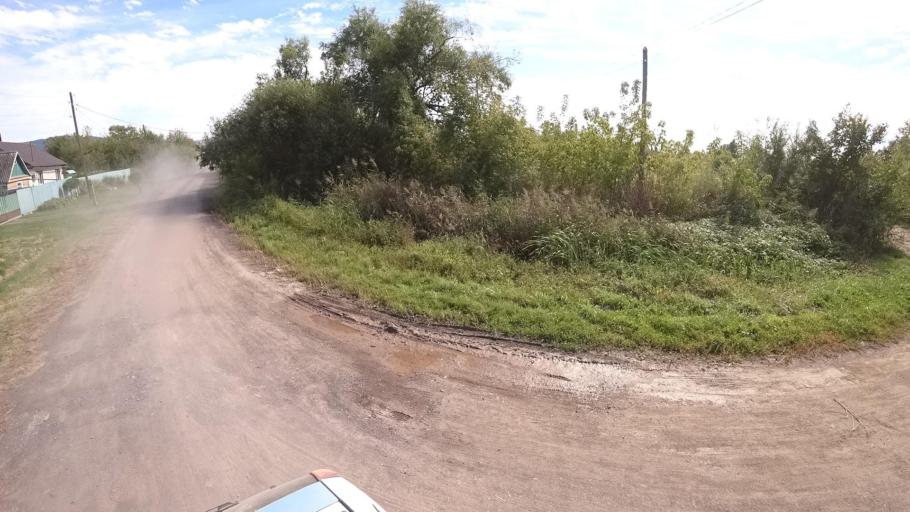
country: RU
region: Primorskiy
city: Yakovlevka
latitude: 44.4351
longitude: 133.5653
